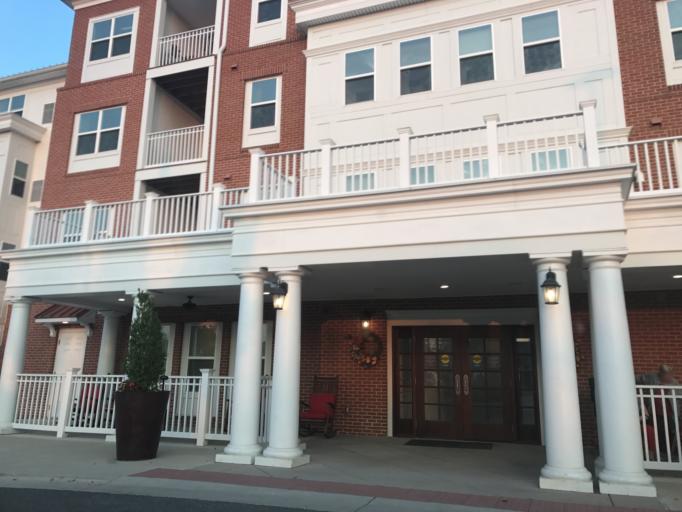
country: US
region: Maryland
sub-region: Baltimore County
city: Perry Hall
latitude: 39.4140
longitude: -76.4585
